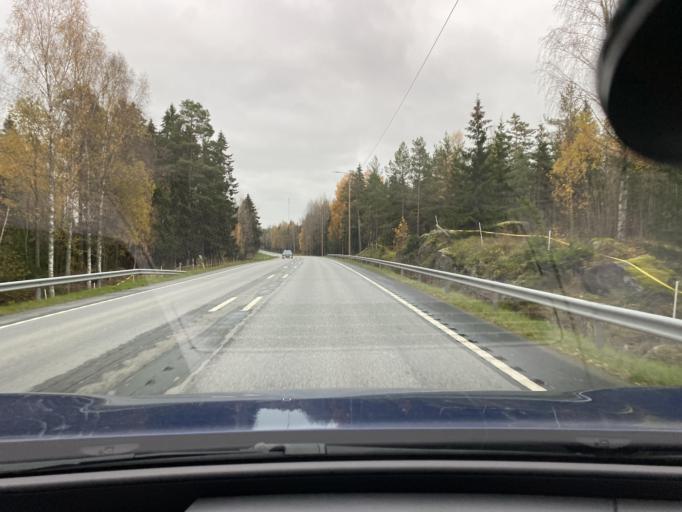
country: FI
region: Varsinais-Suomi
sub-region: Vakka-Suomi
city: Laitila
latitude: 60.9362
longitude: 21.6042
